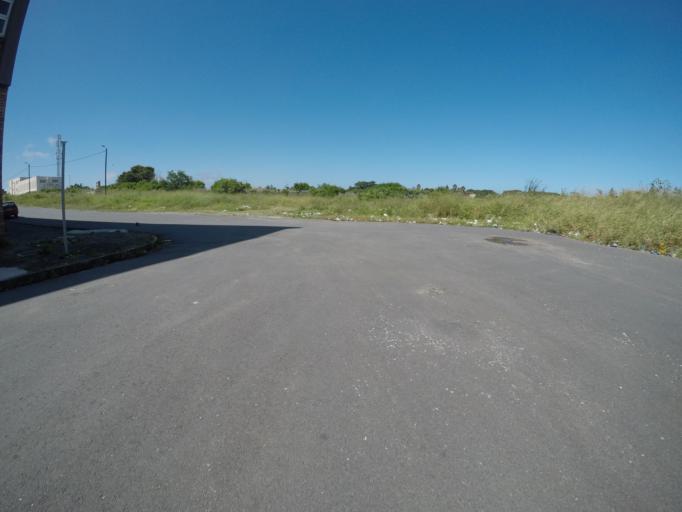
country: ZA
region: Eastern Cape
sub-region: Buffalo City Metropolitan Municipality
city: East London
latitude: -33.0221
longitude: 27.9078
